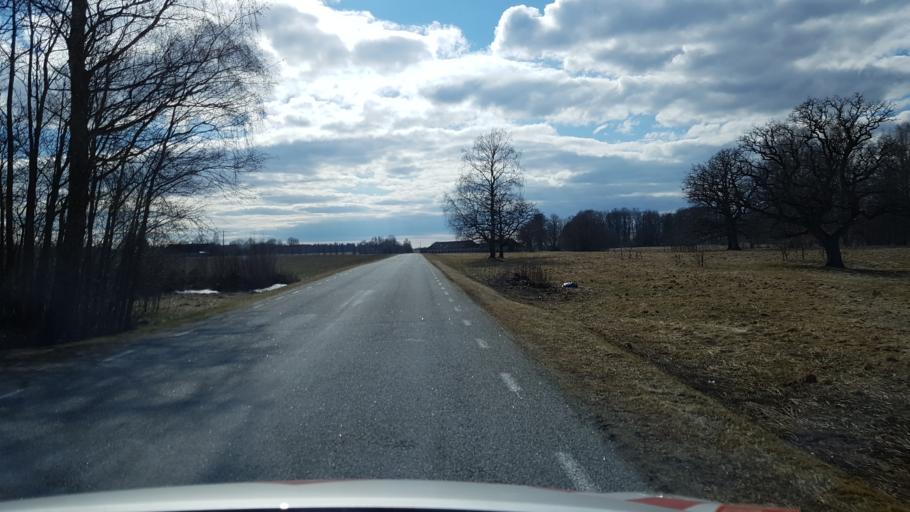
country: EE
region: Laeaene-Virumaa
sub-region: Rakvere linn
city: Rakvere
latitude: 59.3200
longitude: 26.2624
